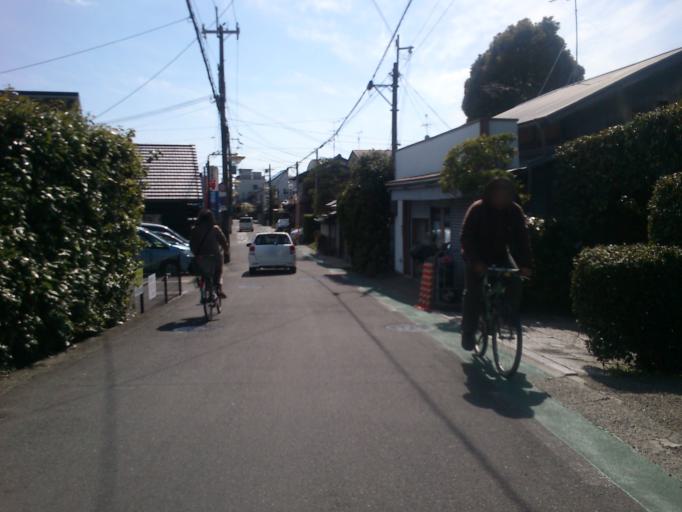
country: JP
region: Kyoto
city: Yawata
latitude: 34.8872
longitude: 135.6710
